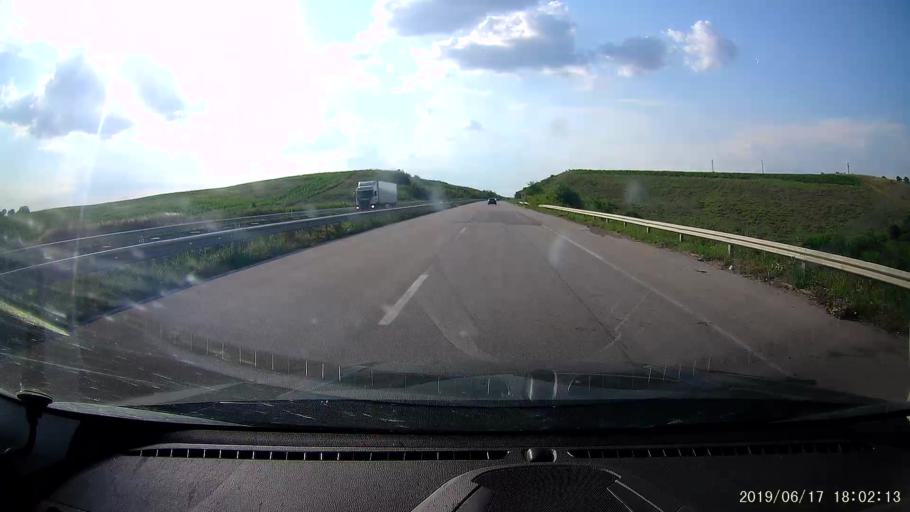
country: BG
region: Khaskovo
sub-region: Obshtina Svilengrad
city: Svilengrad
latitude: 41.7560
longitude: 26.2348
